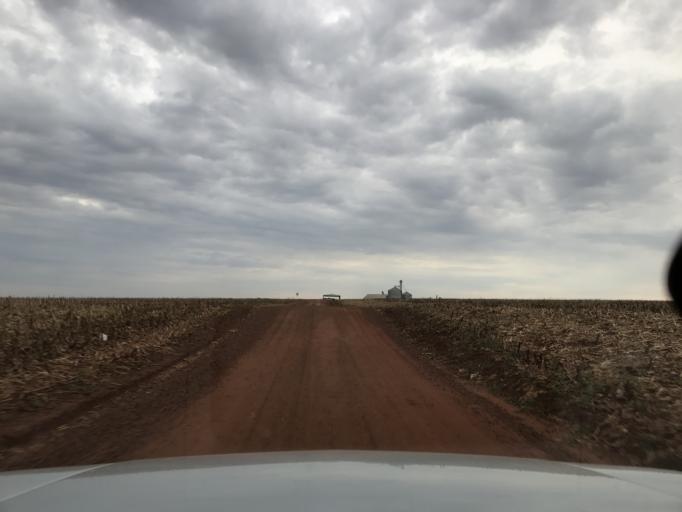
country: BR
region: Parana
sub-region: Palotina
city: Palotina
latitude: -24.2239
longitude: -53.8382
